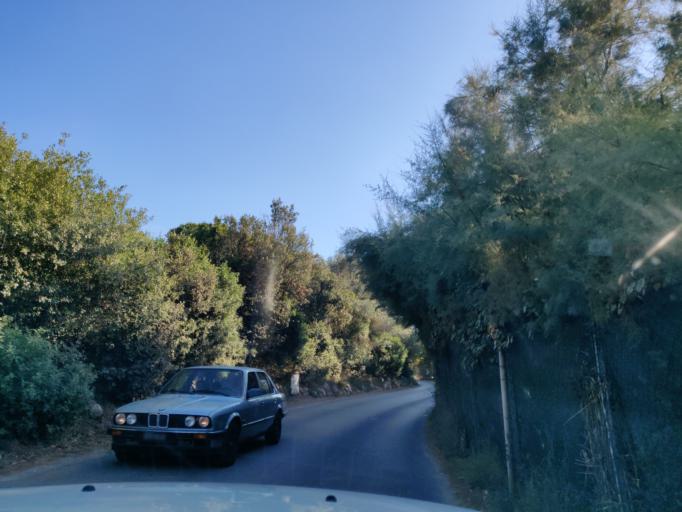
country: IT
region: Tuscany
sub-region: Provincia di Grosseto
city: Orbetello Scalo
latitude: 42.4203
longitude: 11.2824
